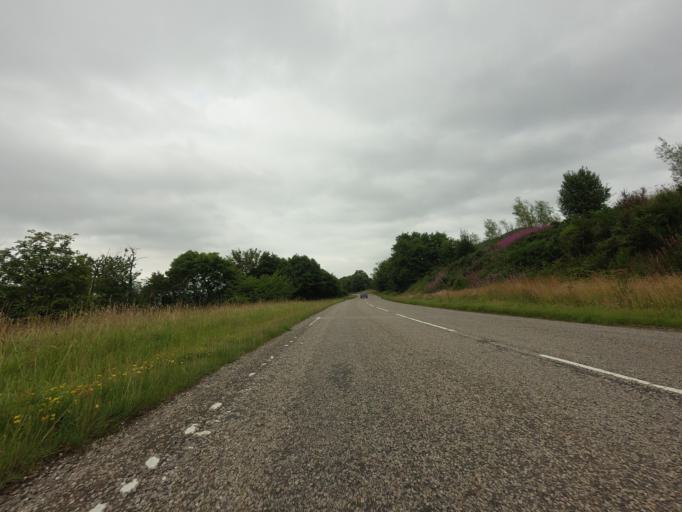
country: GB
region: Scotland
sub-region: Highland
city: Alness
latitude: 57.9104
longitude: -4.3722
